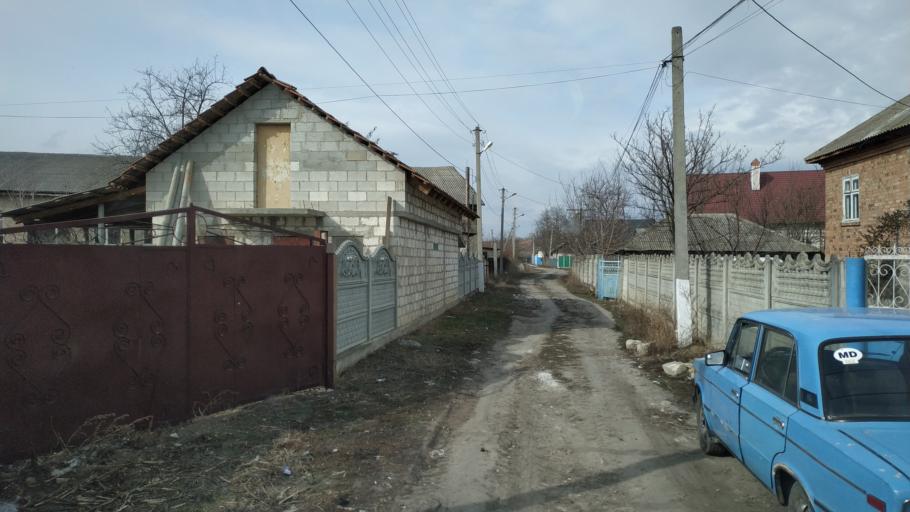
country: MD
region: Laloveni
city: Ialoveni
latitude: 46.8634
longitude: 28.7798
